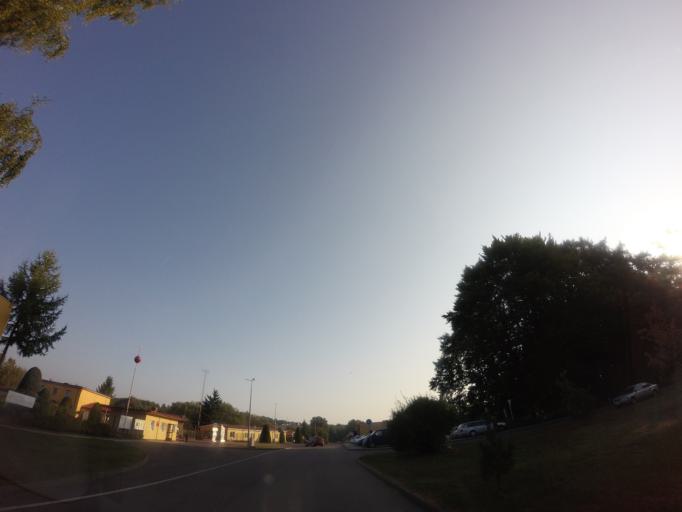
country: PL
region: West Pomeranian Voivodeship
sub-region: Powiat drawski
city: Drawsko Pomorskie
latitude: 53.4716
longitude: 15.7655
